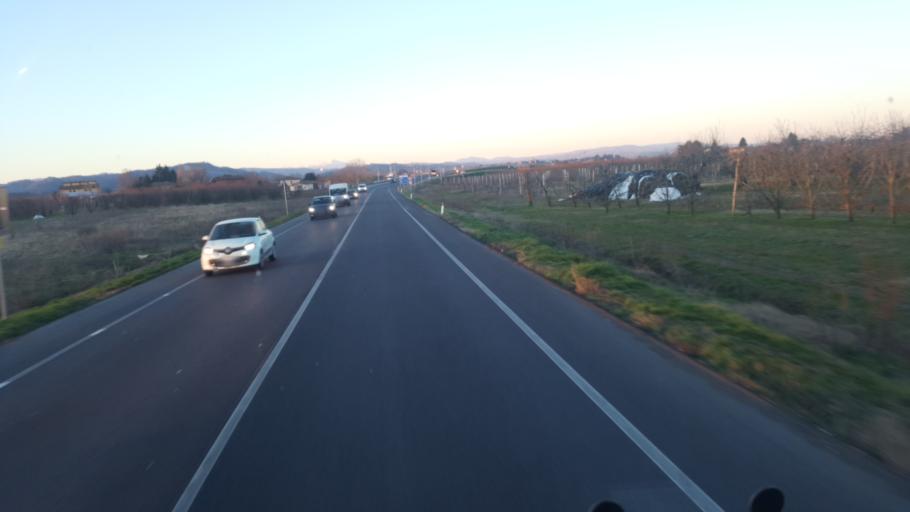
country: IT
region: Emilia-Romagna
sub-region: Provincia di Bologna
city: Crespellano
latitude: 44.5195
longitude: 11.1211
